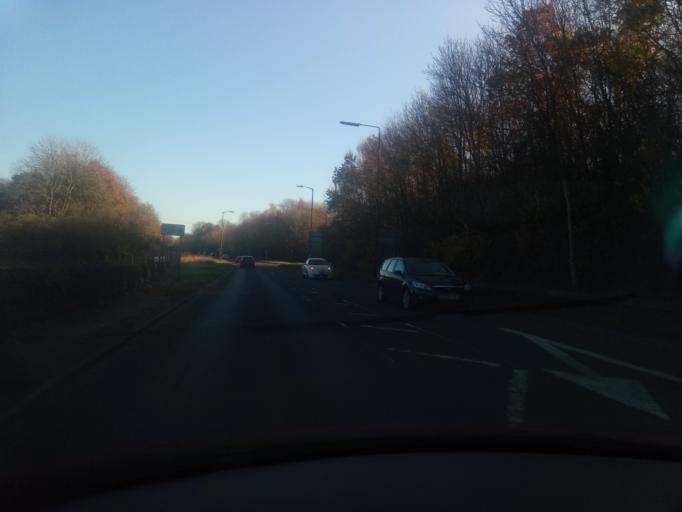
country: GB
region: England
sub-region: Derbyshire
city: Heage
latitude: 53.0614
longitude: -1.4395
